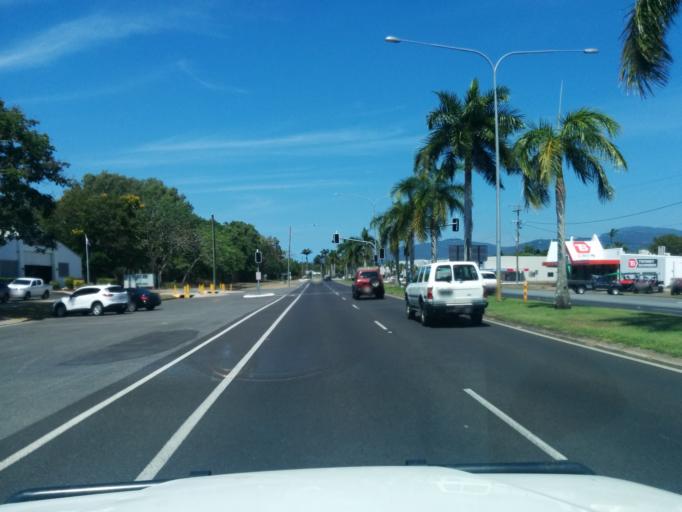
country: AU
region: Queensland
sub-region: Cairns
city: Cairns
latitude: -16.9141
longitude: 145.7509
